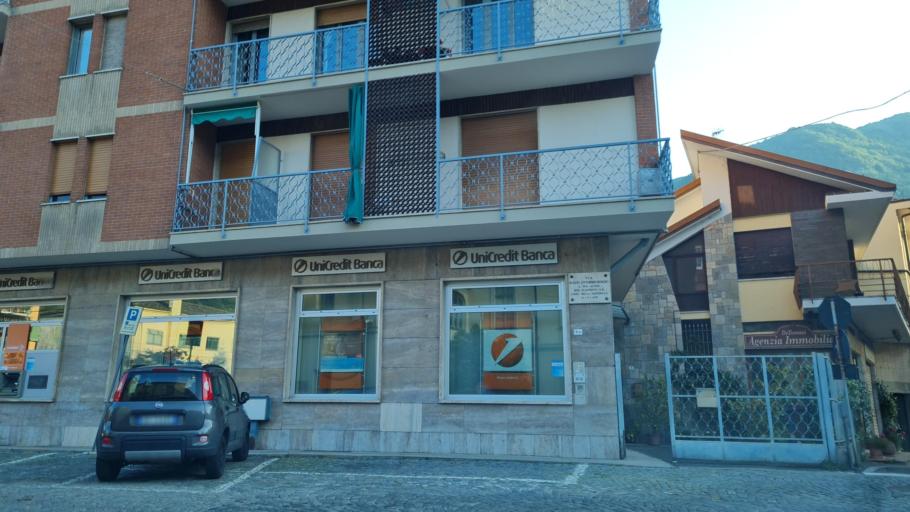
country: IT
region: Piedmont
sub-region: Provincia di Torino
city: Pont-Canavese
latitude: 45.4212
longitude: 7.5948
